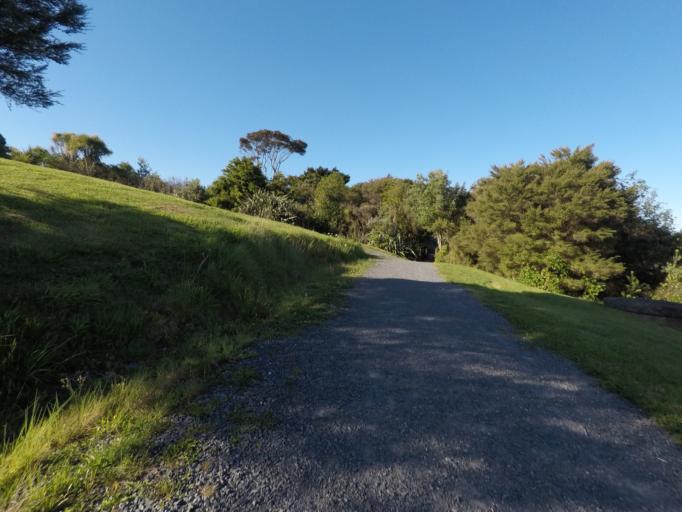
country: NZ
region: Auckland
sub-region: Auckland
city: Rosebank
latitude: -36.8422
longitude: 174.6579
